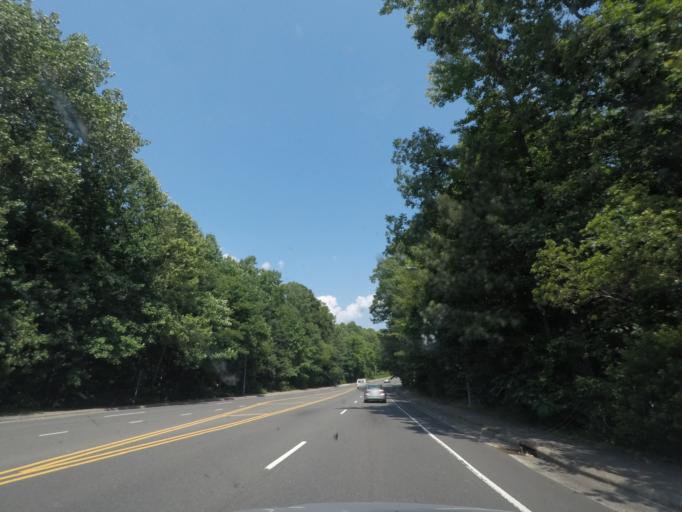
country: US
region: North Carolina
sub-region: Durham County
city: Durham
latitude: 35.9608
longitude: -78.9540
